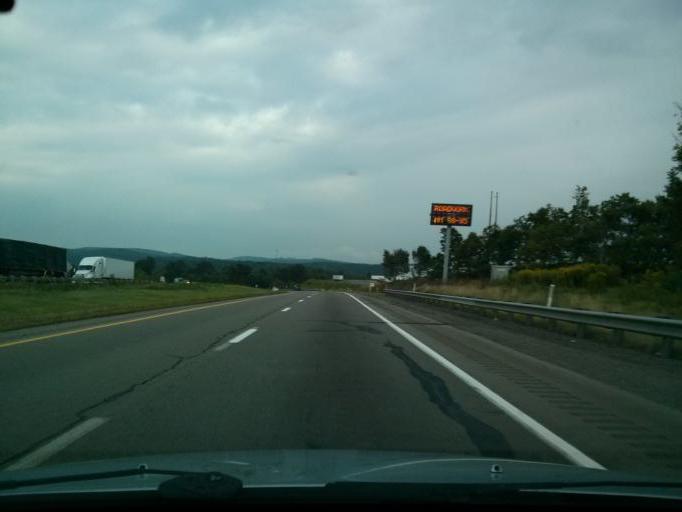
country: US
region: Pennsylvania
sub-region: Jefferson County
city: Brookville
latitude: 41.1679
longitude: -79.0455
